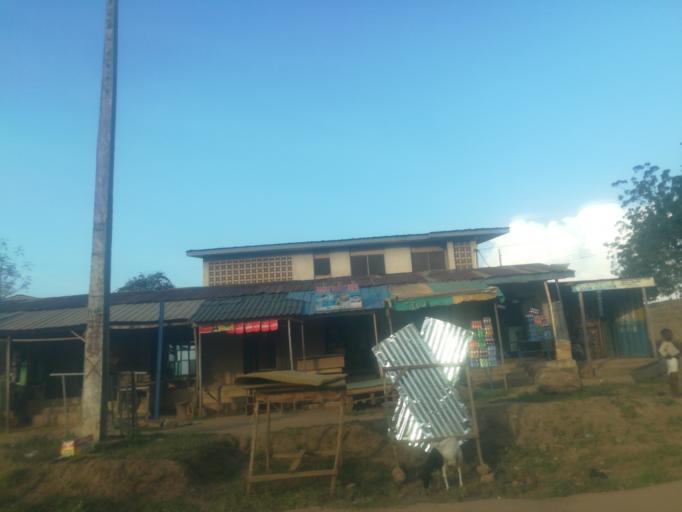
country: NG
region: Oyo
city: Moniya
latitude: 7.5348
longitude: 3.9055
